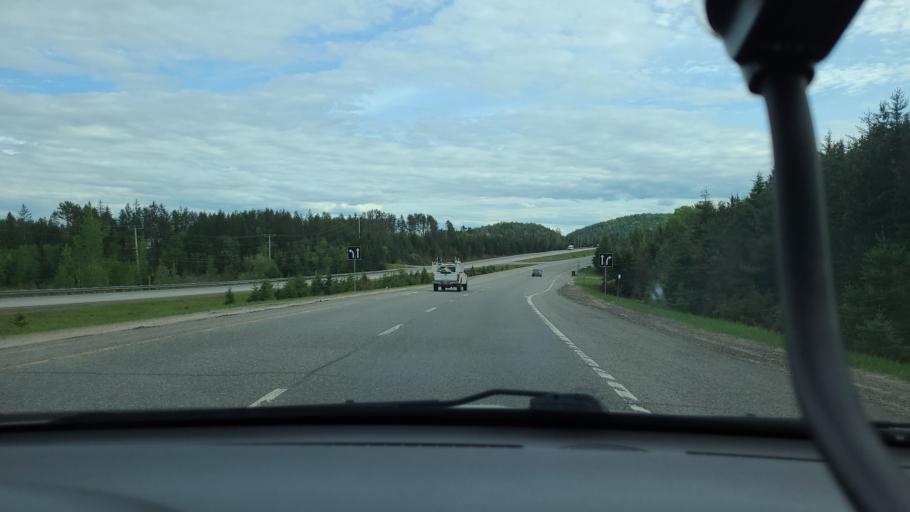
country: CA
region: Quebec
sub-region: Laurentides
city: Labelle
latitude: 46.2429
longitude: -74.7149
